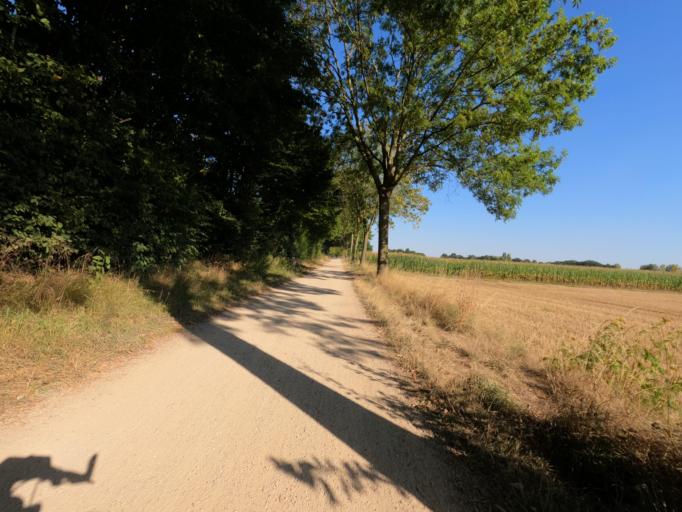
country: NL
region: Limburg
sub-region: Gemeente Roerdalen
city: Vlodrop
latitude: 51.1304
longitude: 6.0909
